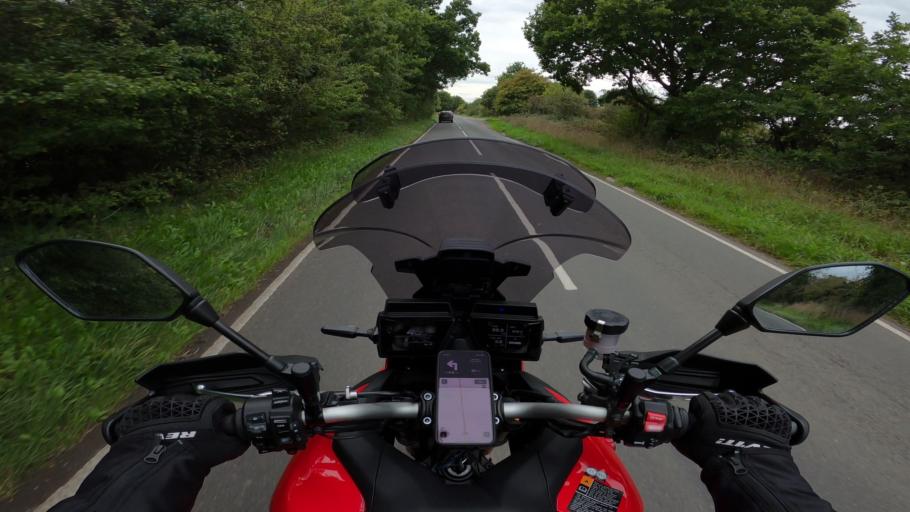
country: GB
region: England
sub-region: Surrey
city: Lingfield
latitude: 51.1862
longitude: -0.0129
